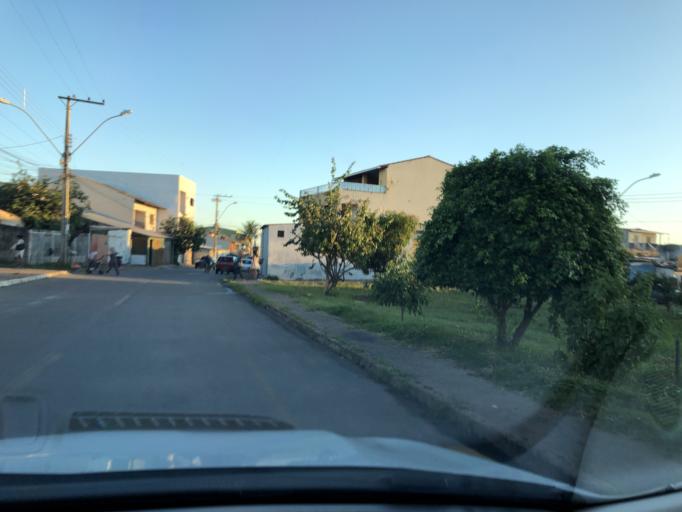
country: BR
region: Federal District
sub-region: Brasilia
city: Brasilia
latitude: -15.7739
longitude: -47.7820
